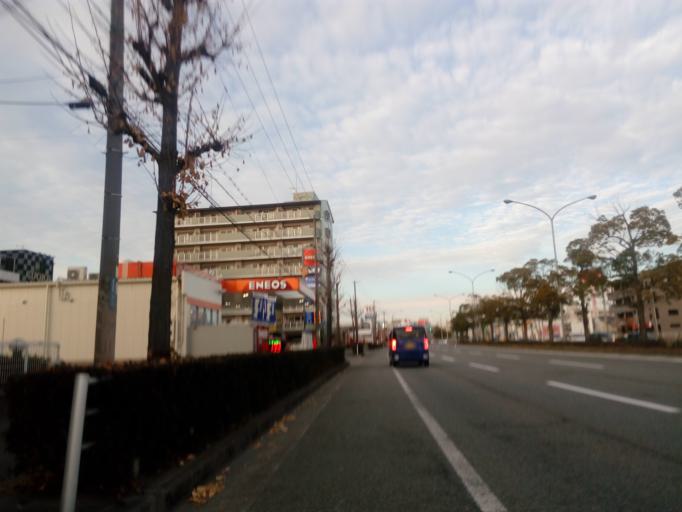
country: JP
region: Hyogo
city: Himeji
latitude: 34.8063
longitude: 134.6803
